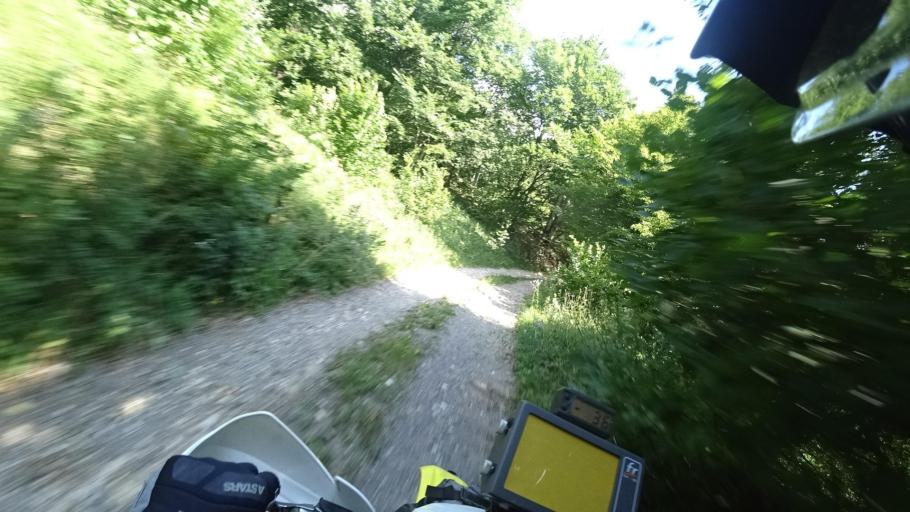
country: HR
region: Karlovacka
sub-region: Grad Ogulin
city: Ogulin
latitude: 45.1760
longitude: 15.1262
